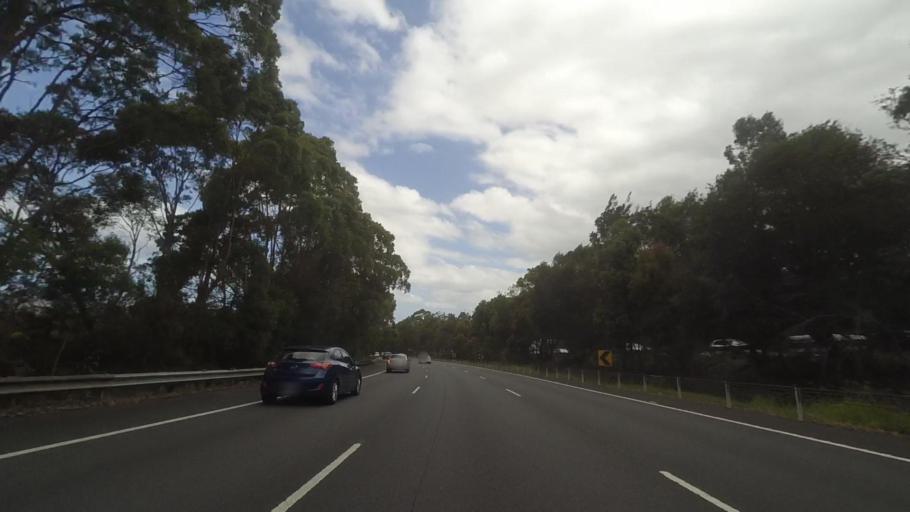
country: AU
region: New South Wales
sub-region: Hornsby Shire
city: Berowra Heights
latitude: -33.5042
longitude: 151.1891
